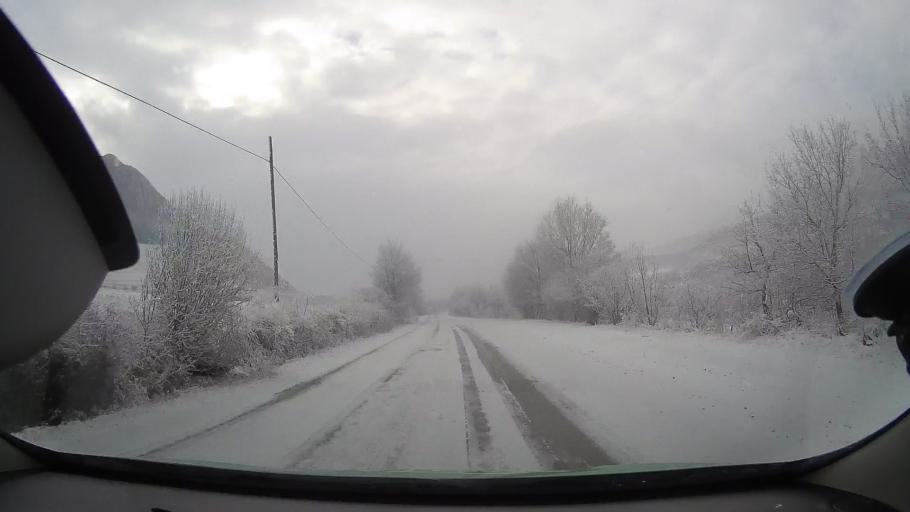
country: RO
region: Alba
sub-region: Comuna Rimetea
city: Rimetea
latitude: 46.4624
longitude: 23.5723
